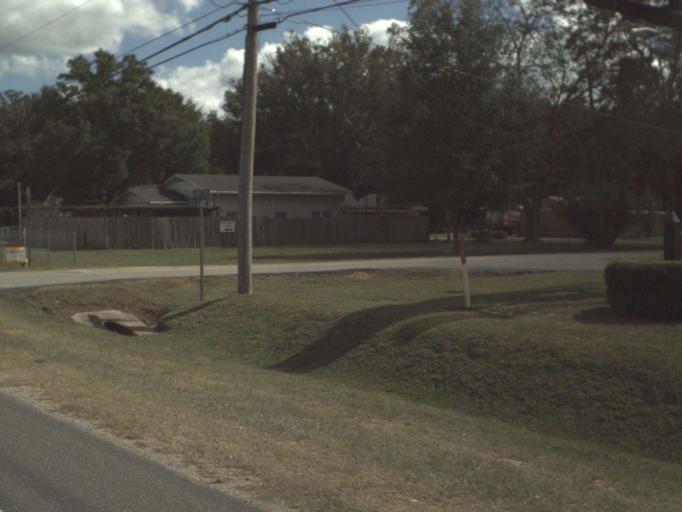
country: US
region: Florida
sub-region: Santa Rosa County
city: Milton
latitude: 30.6027
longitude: -87.0922
